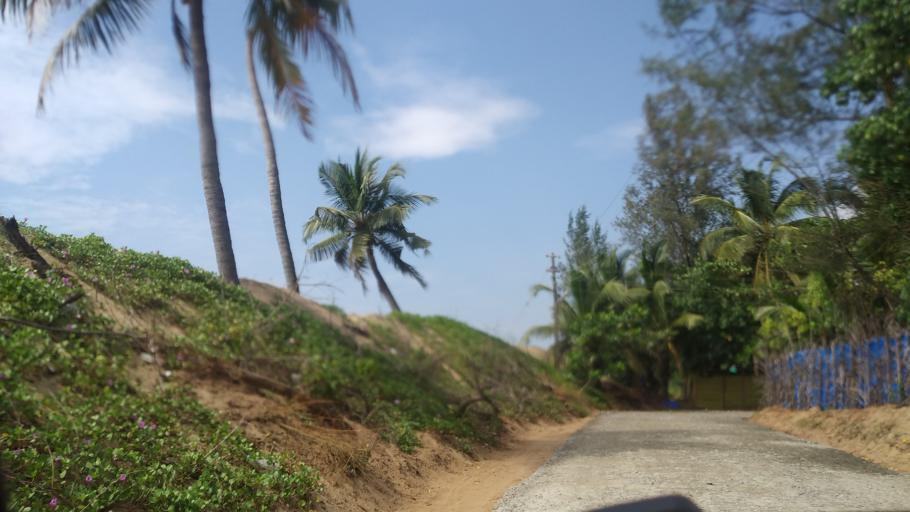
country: IN
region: Kerala
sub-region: Ernakulam
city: Elur
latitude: 10.0637
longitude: 76.1991
